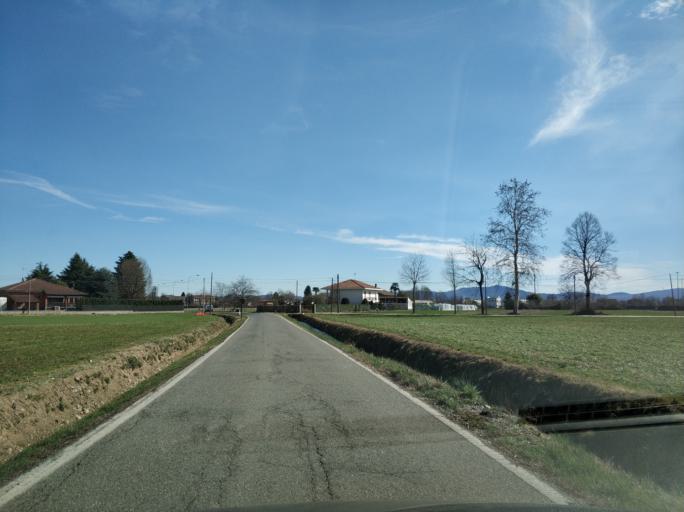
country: IT
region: Piedmont
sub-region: Provincia di Torino
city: Leini
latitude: 45.1894
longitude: 7.7006
